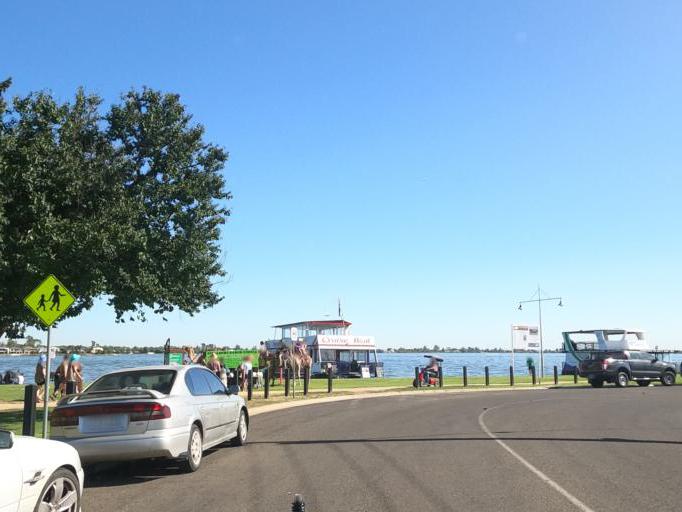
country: AU
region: Victoria
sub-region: Moira
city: Yarrawonga
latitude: -36.0075
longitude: 146.0086
